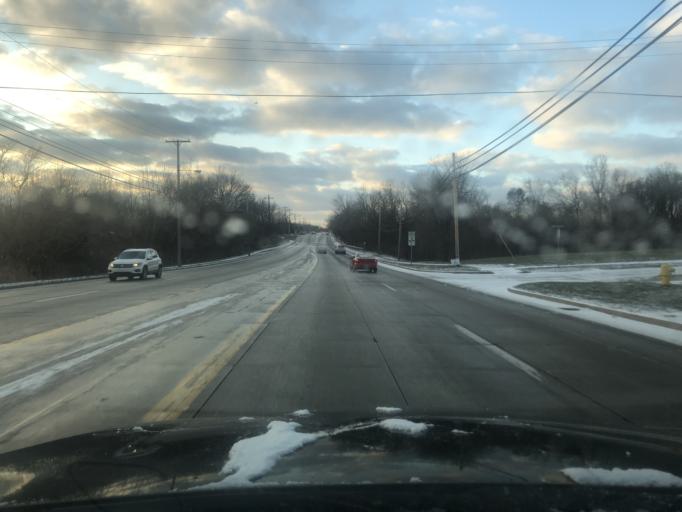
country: US
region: Michigan
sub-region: Wayne County
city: Wayne
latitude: 42.2905
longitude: -83.3490
